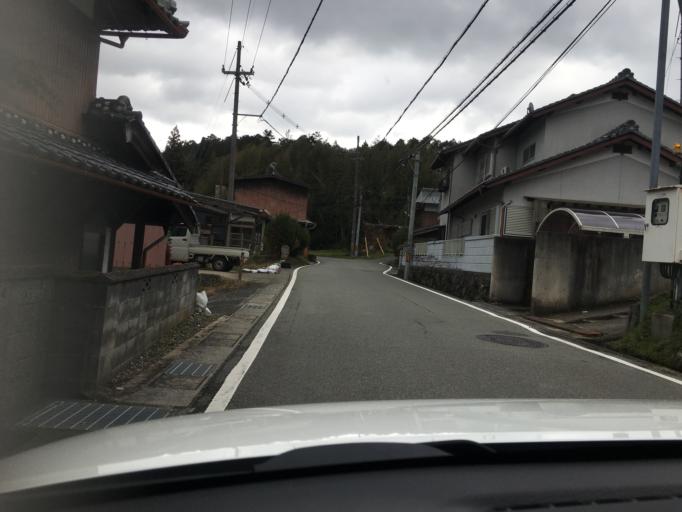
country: JP
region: Kyoto
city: Kameoka
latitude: 35.0422
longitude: 135.4752
